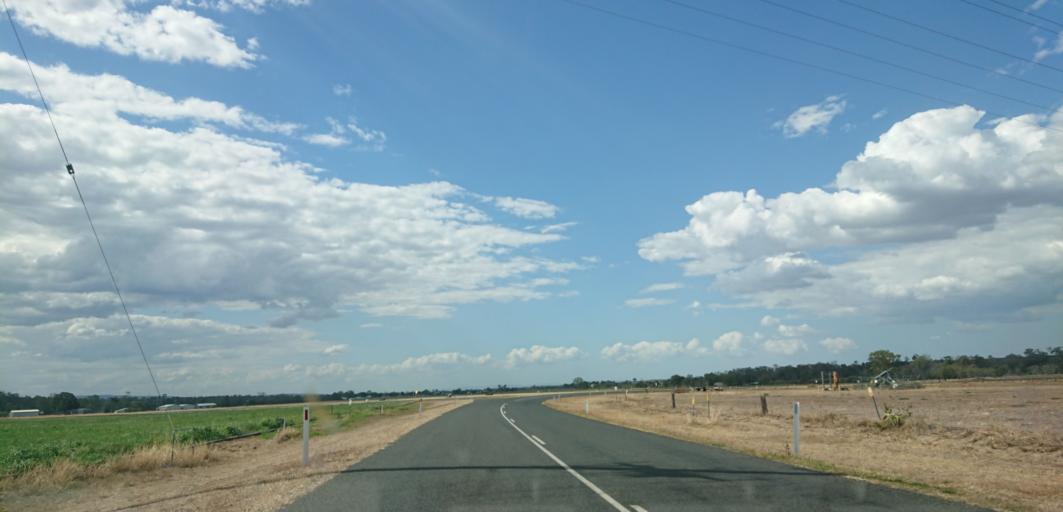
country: AU
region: Queensland
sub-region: Lockyer Valley
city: Gatton
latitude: -27.6264
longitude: 152.1925
